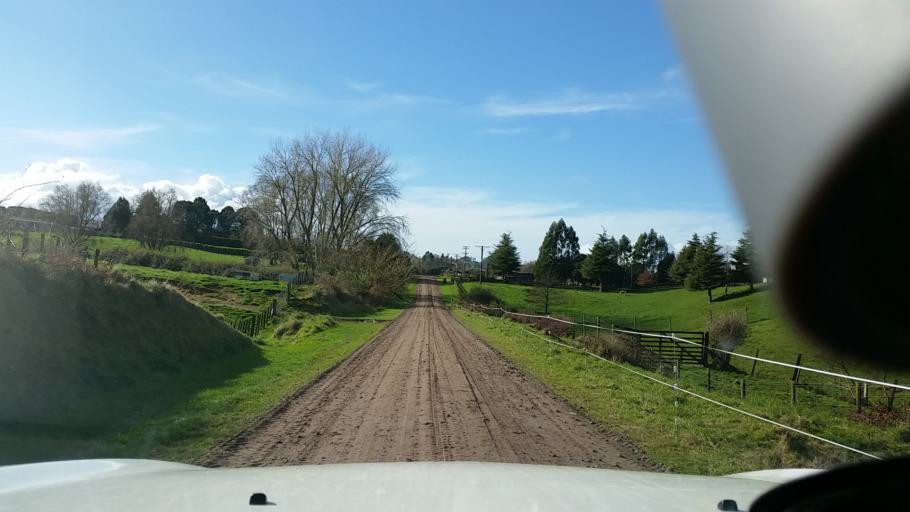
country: NZ
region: Bay of Plenty
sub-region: Rotorua District
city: Rotorua
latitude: -38.0369
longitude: 176.1957
